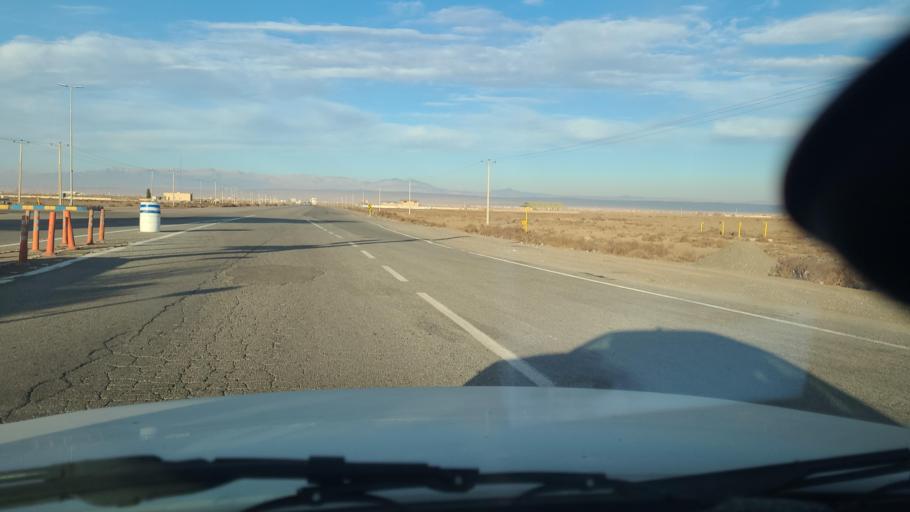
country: IR
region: Razavi Khorasan
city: Neqab
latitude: 36.5850
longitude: 57.5817
